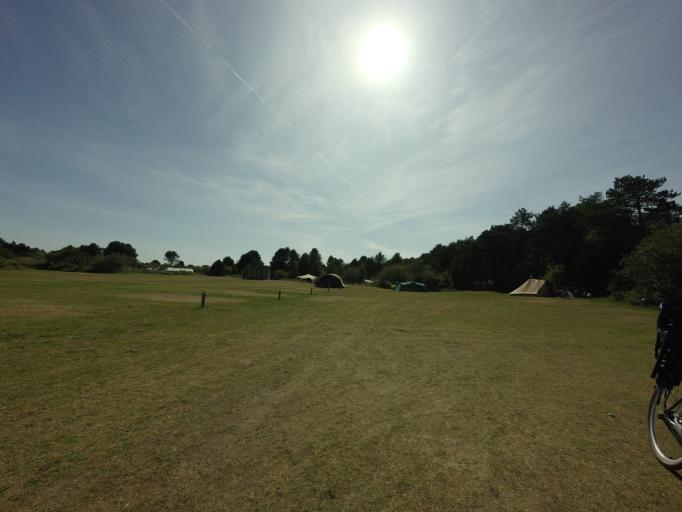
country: NL
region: Friesland
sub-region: Gemeente Ameland
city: Nes
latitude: 53.4541
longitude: 5.7670
